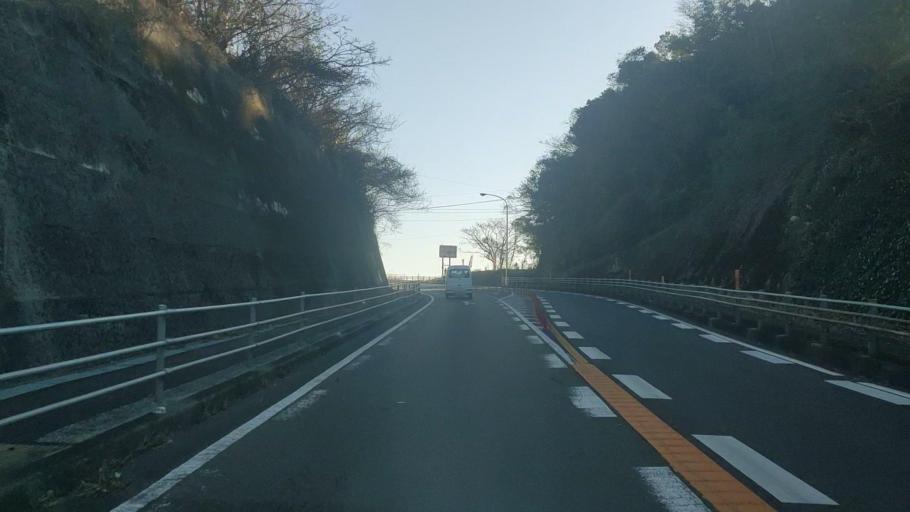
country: JP
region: Miyazaki
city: Takanabe
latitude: 32.3414
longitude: 131.6169
